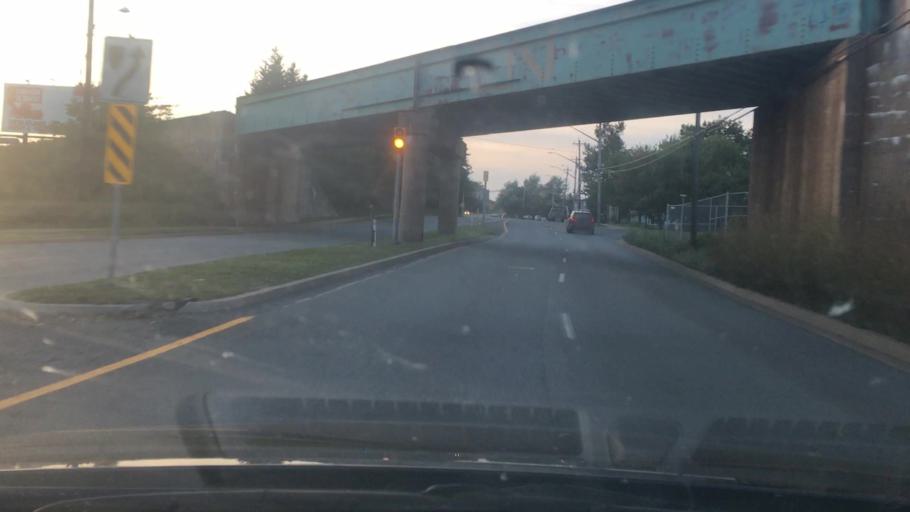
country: CA
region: Nova Scotia
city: Halifax
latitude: 44.6351
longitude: -63.5259
